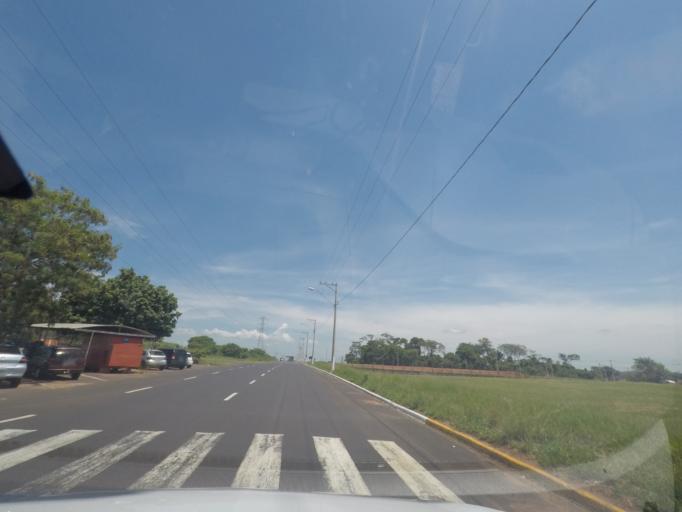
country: BR
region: Sao Paulo
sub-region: Matao
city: Matao
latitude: -21.6108
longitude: -48.3762
